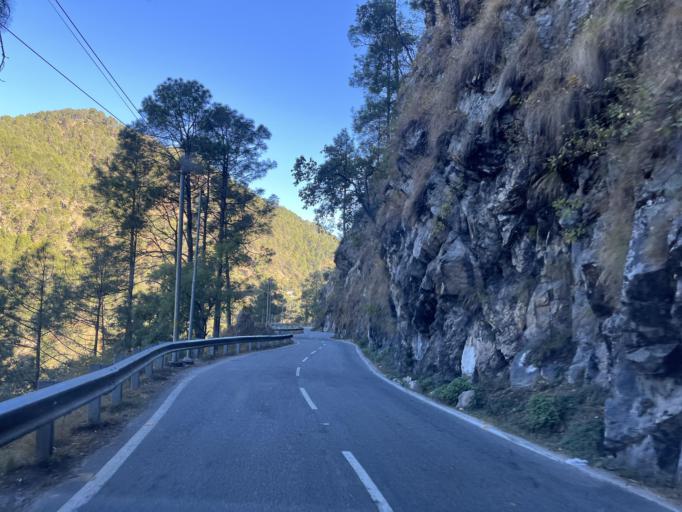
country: IN
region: Uttarakhand
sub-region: Naini Tal
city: Bhowali
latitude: 29.4038
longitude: 79.5102
